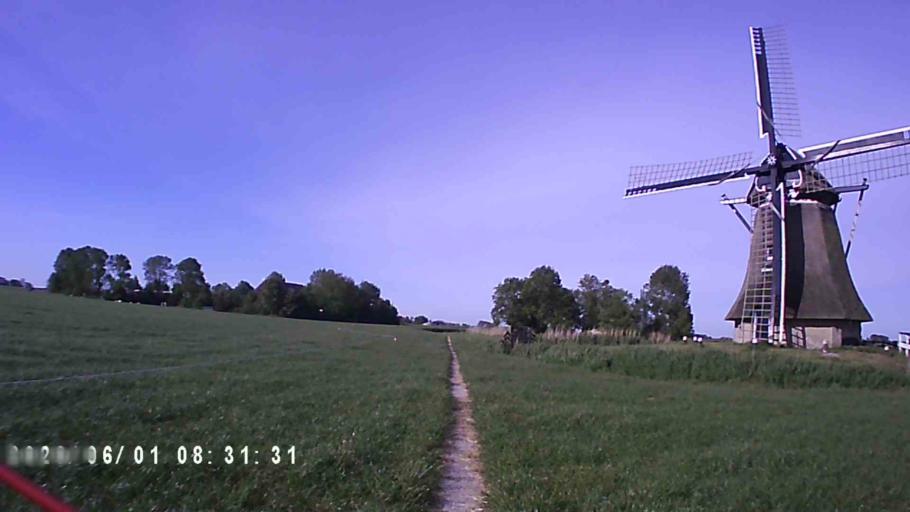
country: NL
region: Friesland
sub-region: Gemeente Ferwerderadiel
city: Burdaard
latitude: 53.3000
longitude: 5.8492
